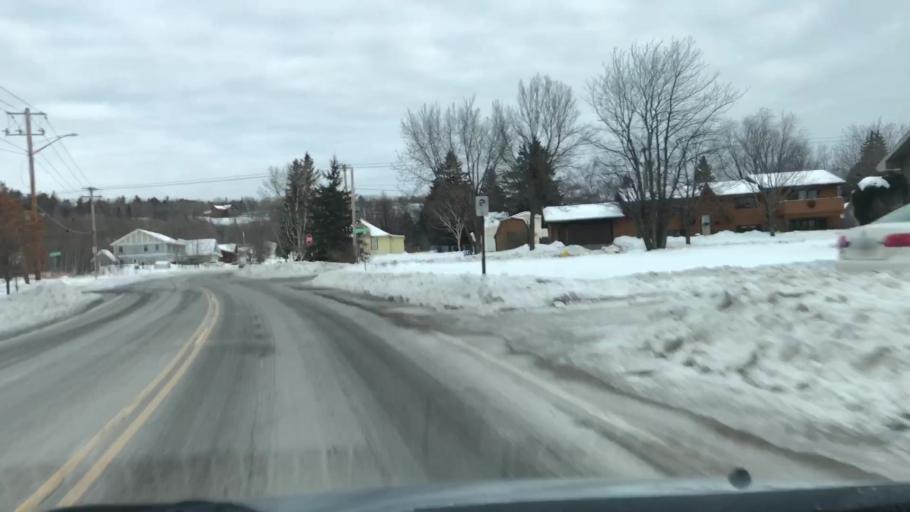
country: US
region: Minnesota
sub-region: Saint Louis County
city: Arnold
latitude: 46.8359
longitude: -92.0368
